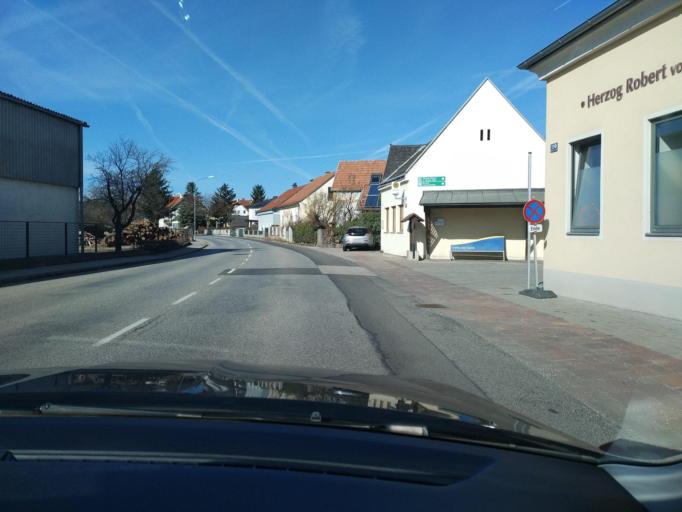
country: AT
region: Lower Austria
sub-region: Politischer Bezirk Neunkirchen
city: Pitten
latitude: 47.7318
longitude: 16.1688
